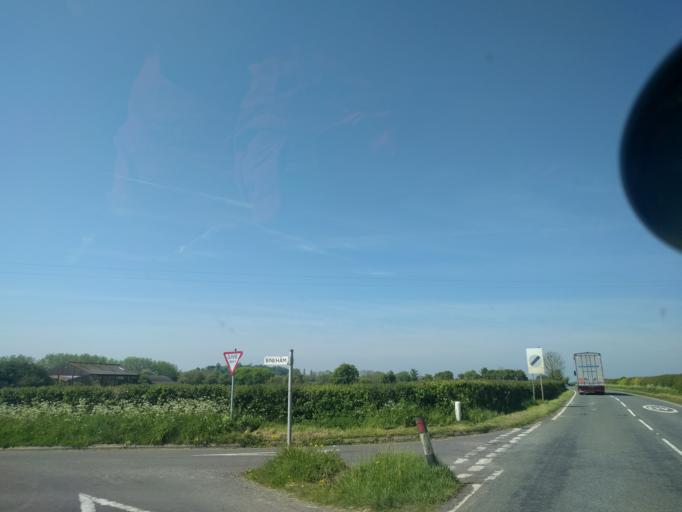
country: GB
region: England
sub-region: Somerset
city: Ilchester
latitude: 51.0295
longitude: -2.7282
